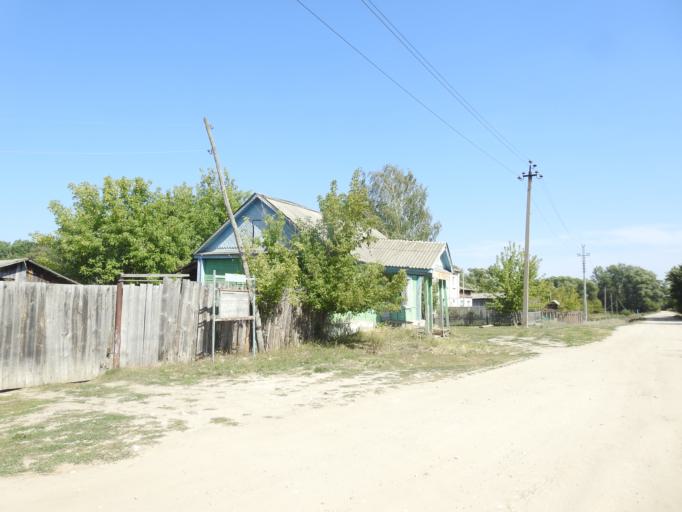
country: RU
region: Saratov
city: Lysyye Gory
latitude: 51.3115
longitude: 45.0104
